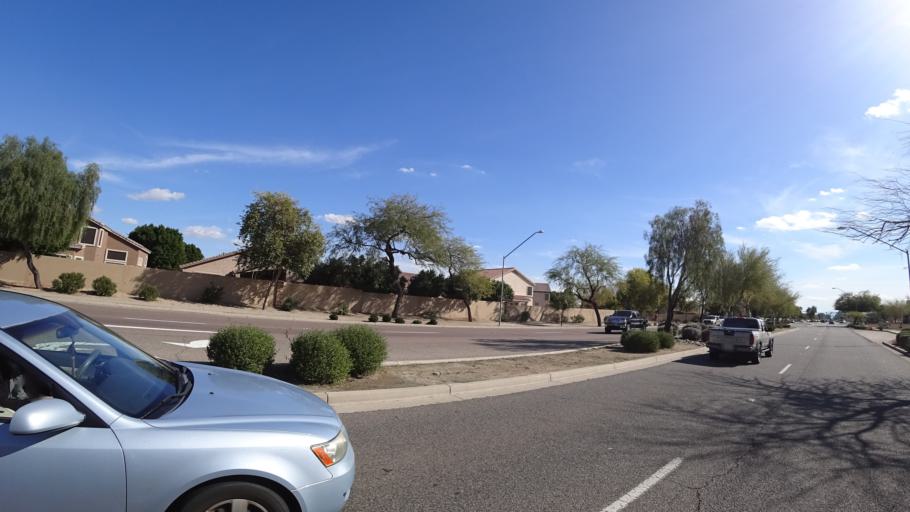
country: US
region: Arizona
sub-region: Maricopa County
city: Sun City
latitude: 33.6737
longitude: -112.2204
